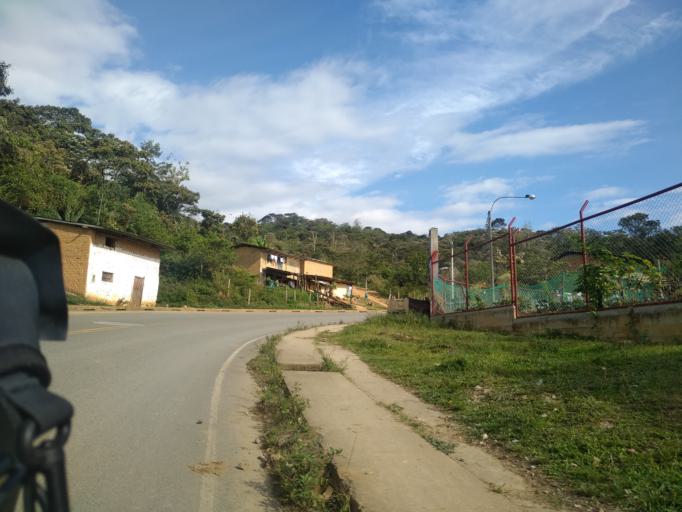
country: PE
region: Cajamarca
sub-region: Provincia de San Ignacio
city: San Ignacio
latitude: -5.0989
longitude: -79.0448
